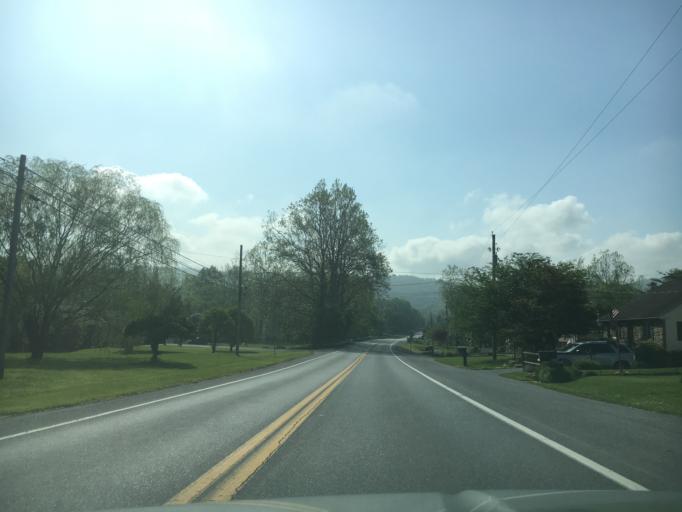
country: US
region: Pennsylvania
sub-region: Berks County
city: Oley
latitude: 40.3835
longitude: -75.7314
